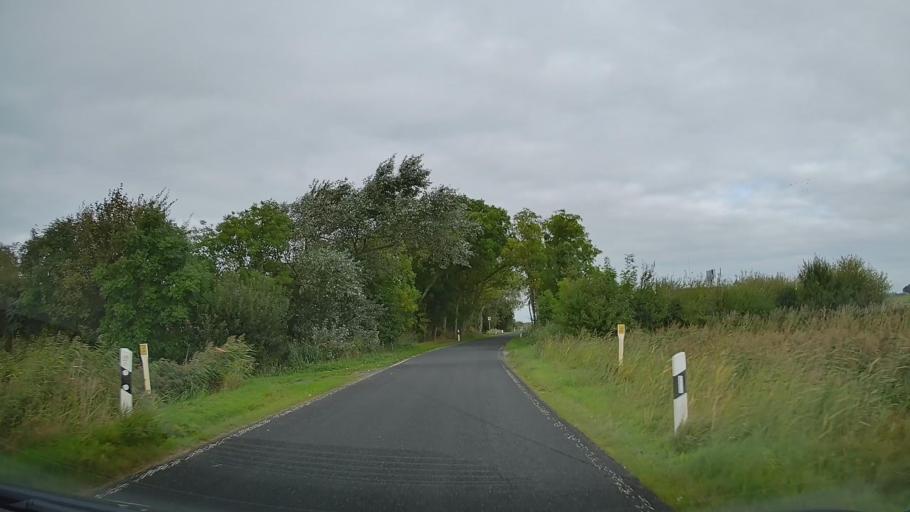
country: DE
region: Schleswig-Holstein
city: Emmelsbull-Horsbull
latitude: 54.8162
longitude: 8.6521
